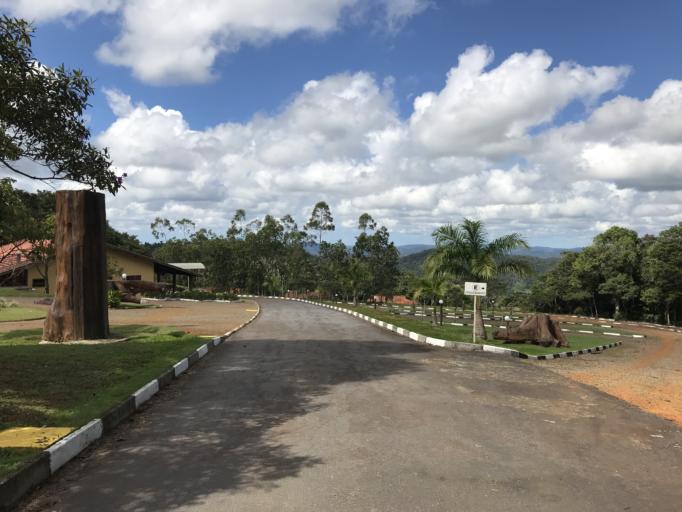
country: BR
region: Bahia
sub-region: Gandu
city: Gandu
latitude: -13.8979
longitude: -39.4579
